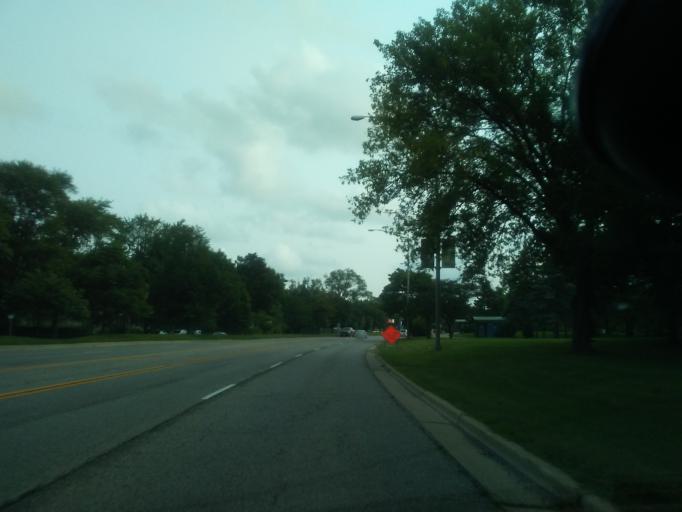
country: US
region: Illinois
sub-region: Cook County
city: Evanston
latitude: 42.0504
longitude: -87.7103
